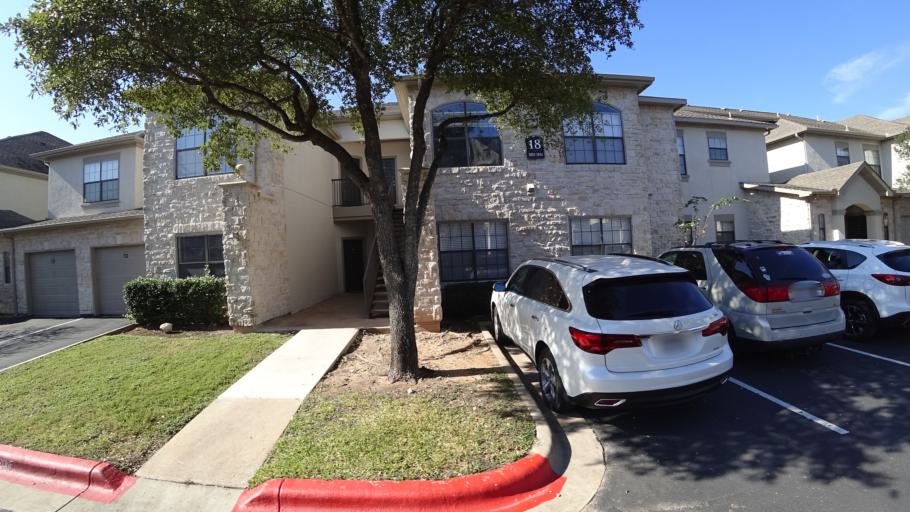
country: US
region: Texas
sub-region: Williamson County
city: Jollyville
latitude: 30.3774
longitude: -97.7705
